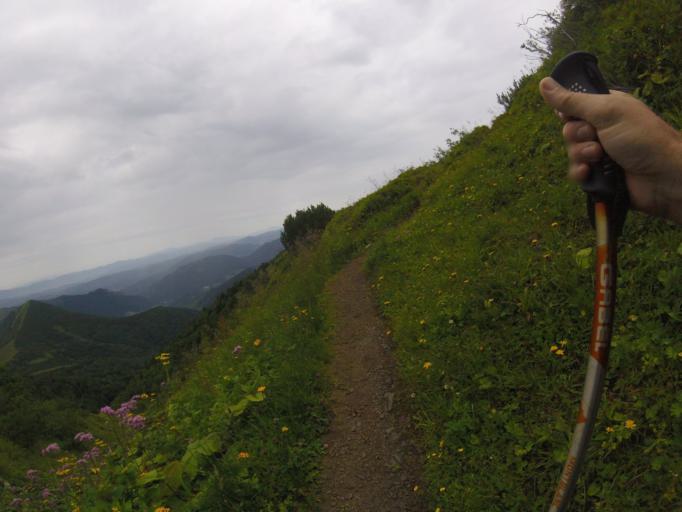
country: SK
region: Zilinsky
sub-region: Okres Zilina
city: Terchova
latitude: 49.1933
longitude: 19.0185
